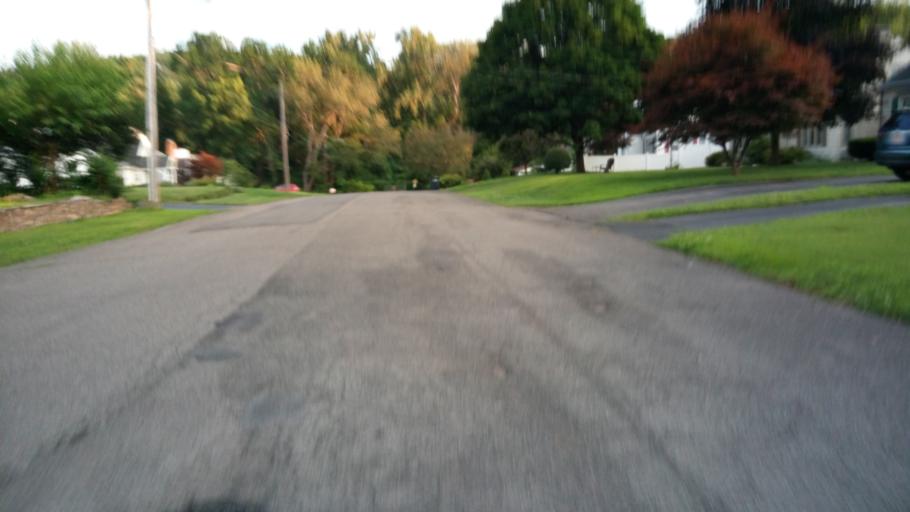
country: US
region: New York
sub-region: Chemung County
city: West Elmira
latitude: 42.0765
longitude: -76.8500
